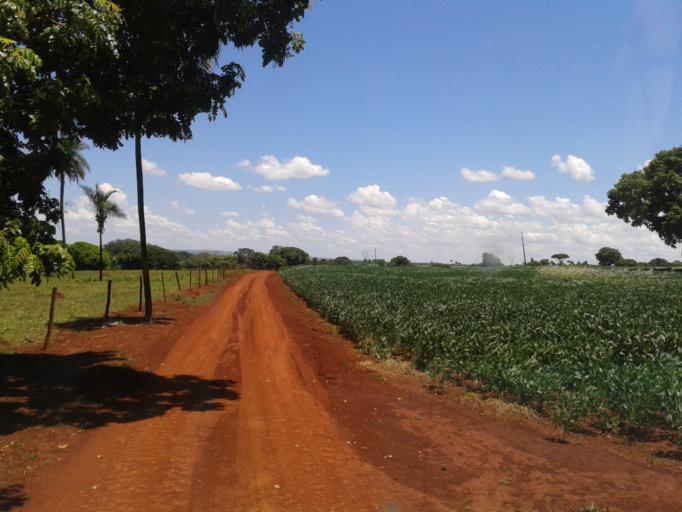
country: BR
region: Minas Gerais
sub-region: Centralina
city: Centralina
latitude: -18.6253
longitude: -49.2956
